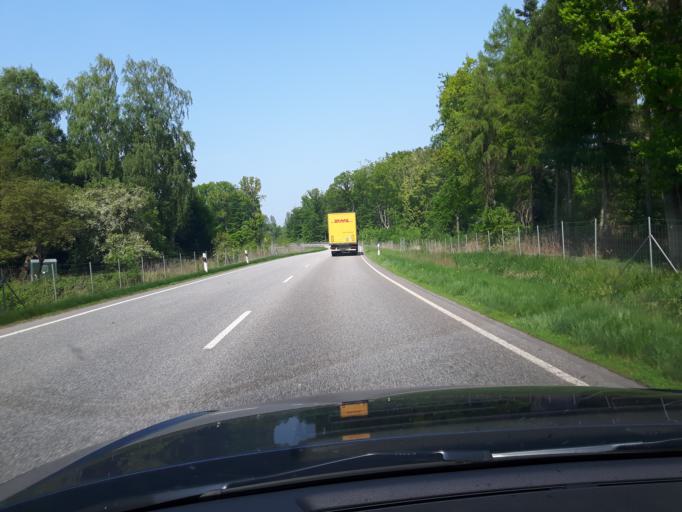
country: DE
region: Schleswig-Holstein
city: Ratekau
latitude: 53.8859
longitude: 10.7681
